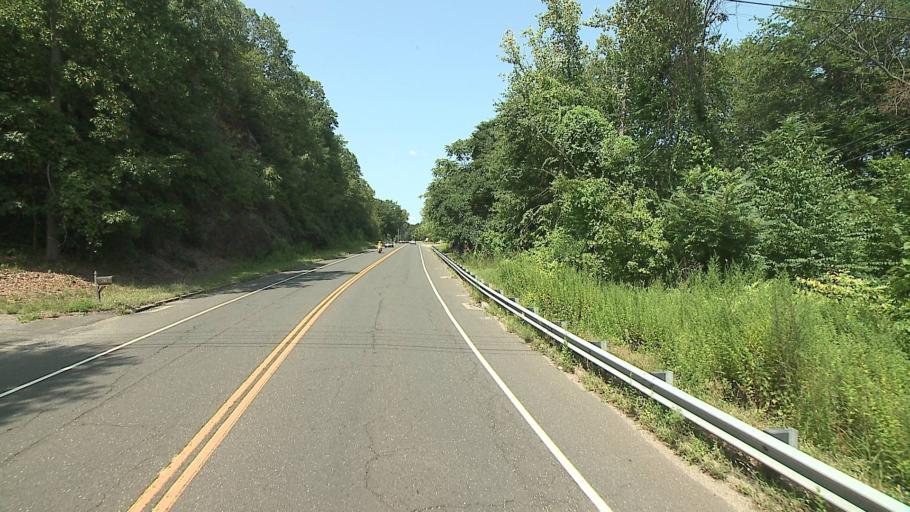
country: US
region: Connecticut
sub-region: New Haven County
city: Derby
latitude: 41.3051
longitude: -73.0776
